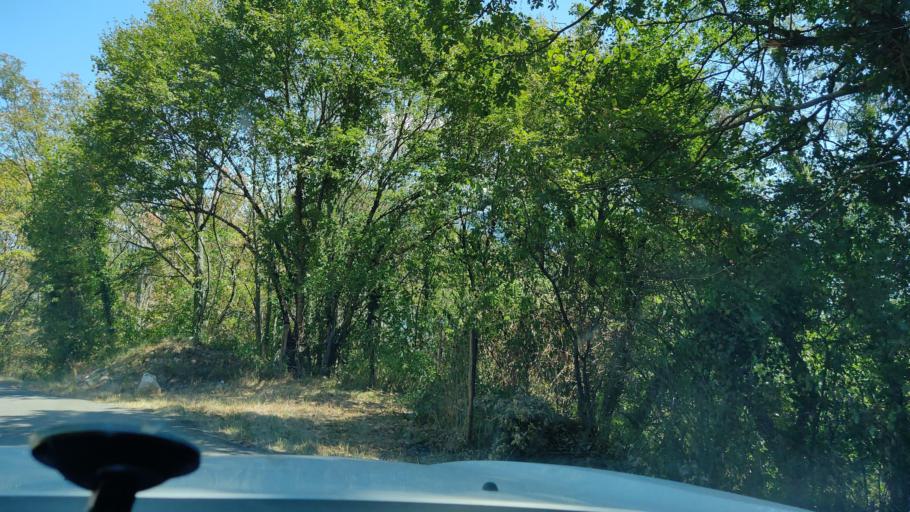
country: FR
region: Rhone-Alpes
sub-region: Departement de la Savoie
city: Le Bourget-du-Lac
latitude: 45.6530
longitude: 5.8465
